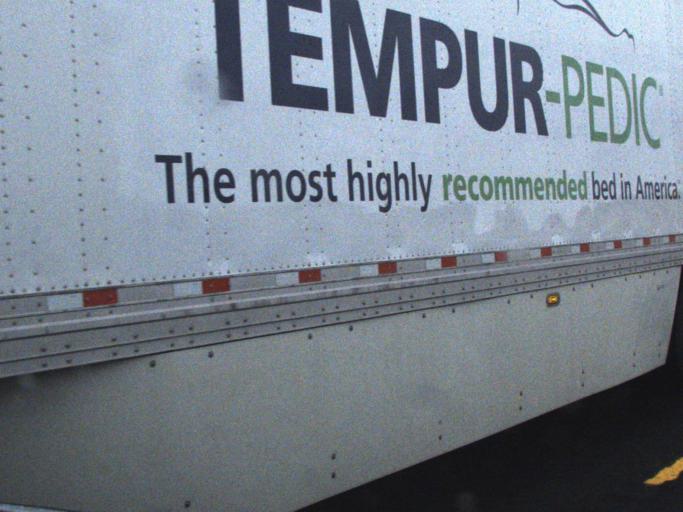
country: US
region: Washington
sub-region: Adams County
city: Ritzville
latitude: 46.7721
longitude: -118.1128
